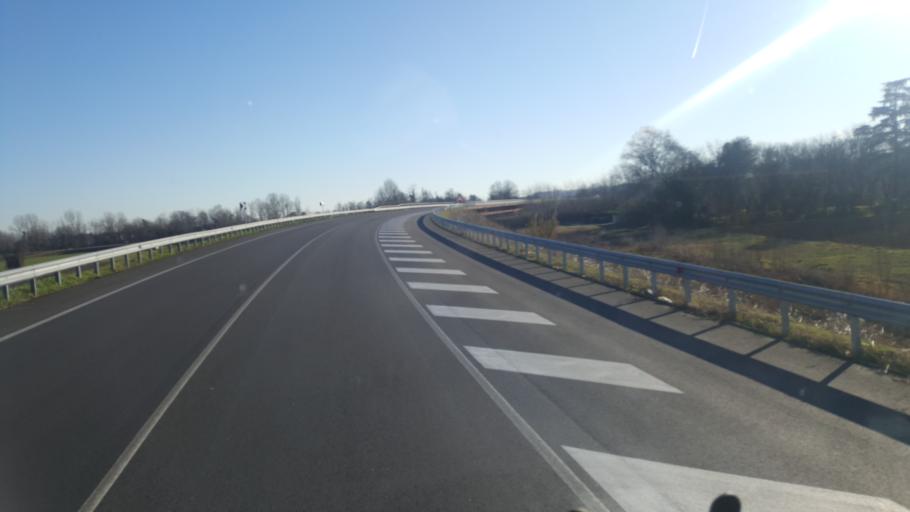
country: IT
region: Emilia-Romagna
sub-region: Provincia di Bologna
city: Bazzano
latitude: 44.5142
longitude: 11.0756
